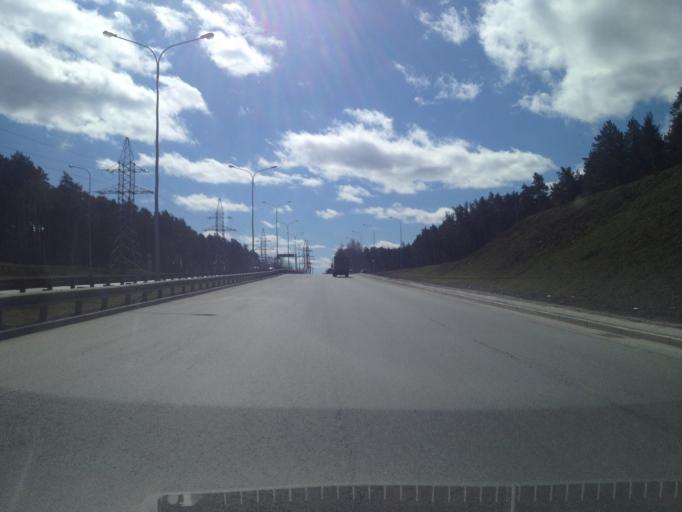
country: RU
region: Sverdlovsk
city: Sovkhoznyy
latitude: 56.7884
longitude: 60.5977
